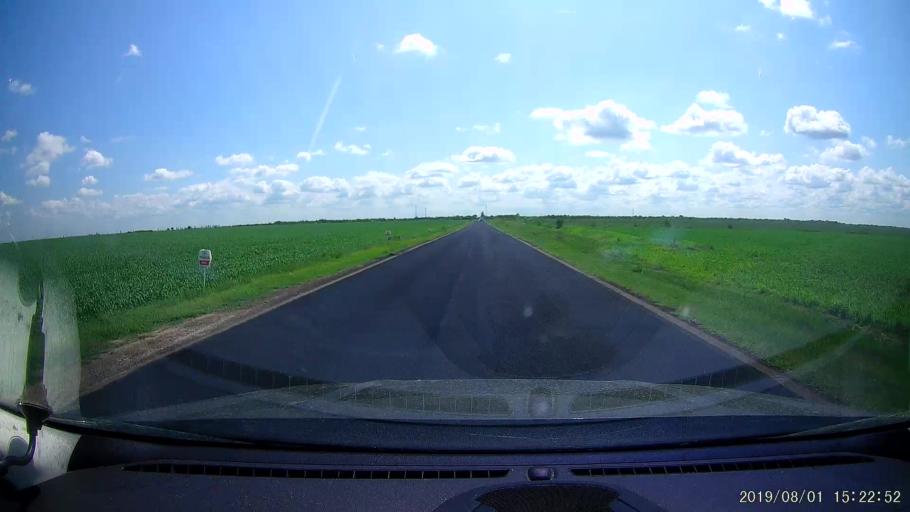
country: RO
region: Braila
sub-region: Comuna Viziru
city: Lanurile
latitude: 45.0483
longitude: 27.7697
